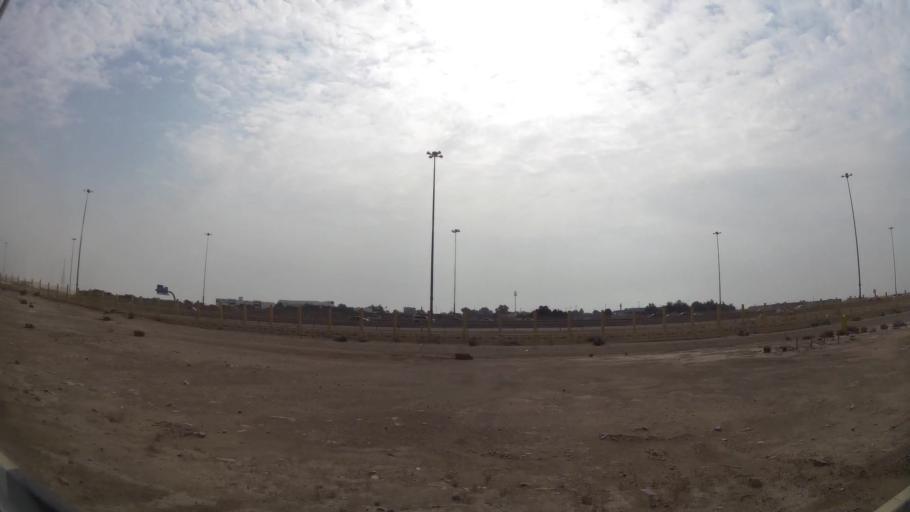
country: AE
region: Abu Dhabi
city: Abu Dhabi
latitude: 24.6828
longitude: 54.7690
